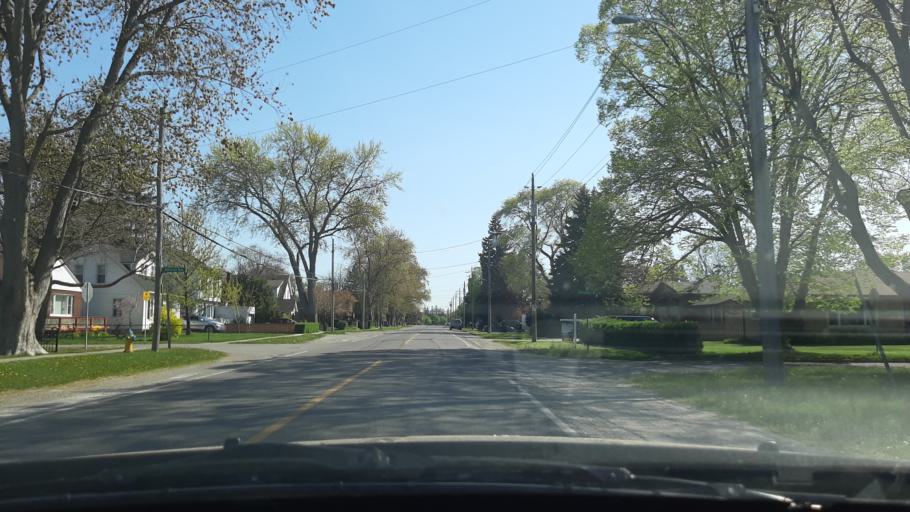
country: CA
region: Ontario
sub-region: Regional Municipality of Niagara
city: St. Catharines
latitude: 43.2088
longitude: -79.2188
